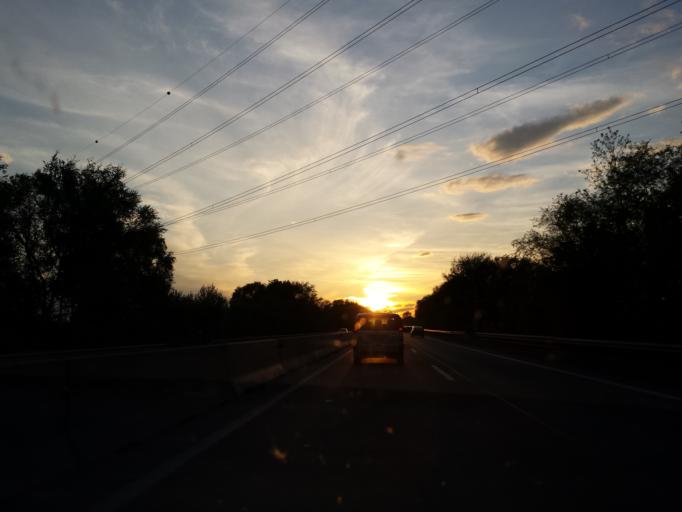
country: AT
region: Lower Austria
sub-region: Politischer Bezirk Bruck an der Leitha
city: Bruck an der Leitha
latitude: 48.0458
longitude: 16.7488
